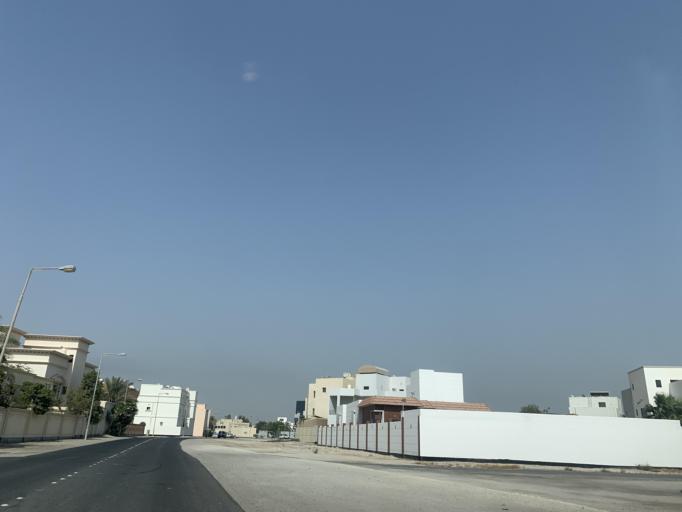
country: BH
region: Manama
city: Jidd Hafs
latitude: 26.2078
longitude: 50.5292
